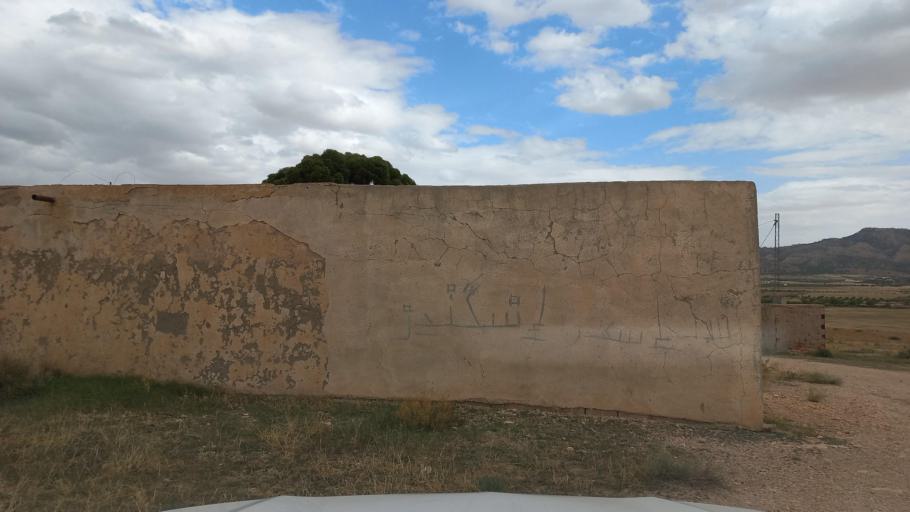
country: TN
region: Al Qasrayn
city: Sbiba
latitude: 35.3785
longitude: 9.1292
